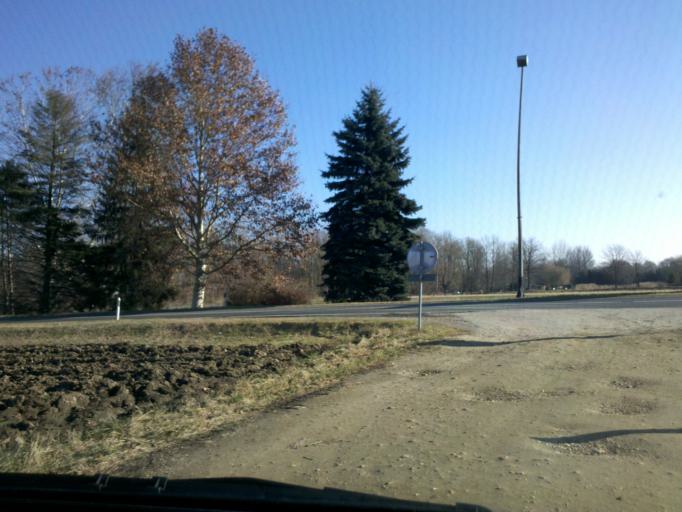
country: HR
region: Medimurska
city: Gorican
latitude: 46.4128
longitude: 16.6888
